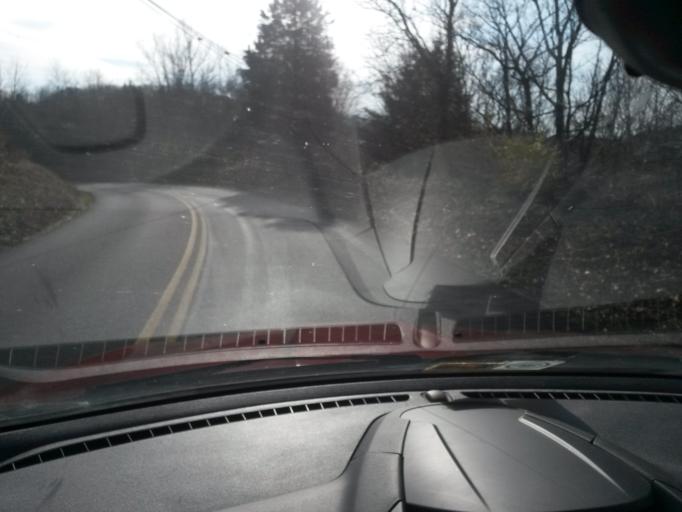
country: US
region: Virginia
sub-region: Botetourt County
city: Fincastle
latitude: 37.5207
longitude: -79.8797
